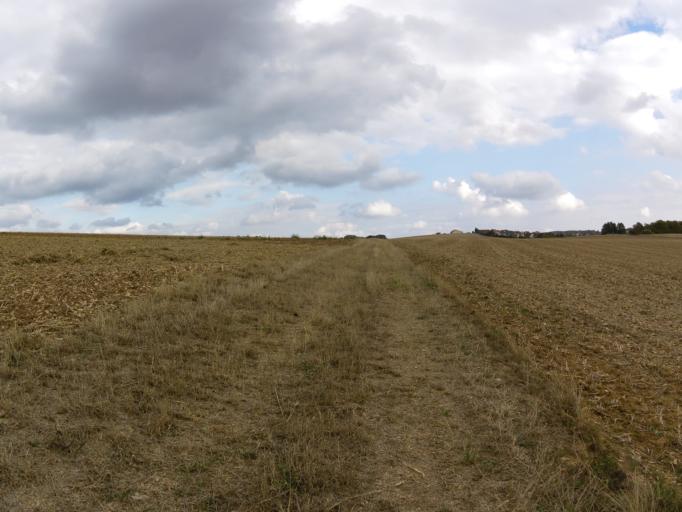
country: DE
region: Bavaria
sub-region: Regierungsbezirk Unterfranken
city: Waldbrunn
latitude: 49.7670
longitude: 9.8119
